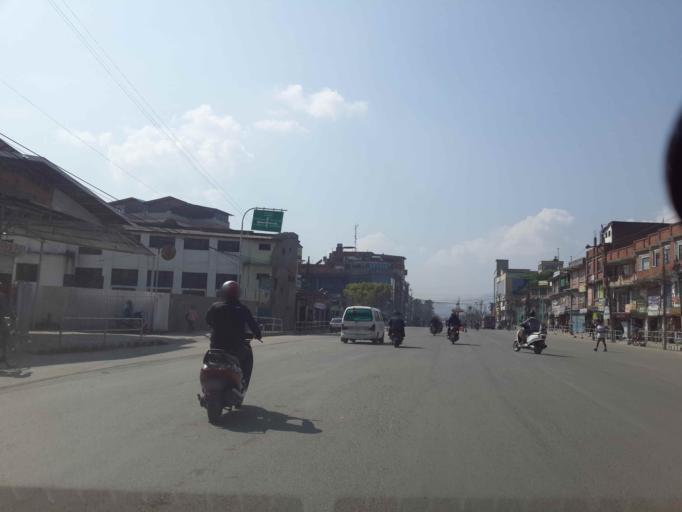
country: NP
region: Central Region
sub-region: Bagmati Zone
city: Kathmandu
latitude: 27.7395
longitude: 85.3382
